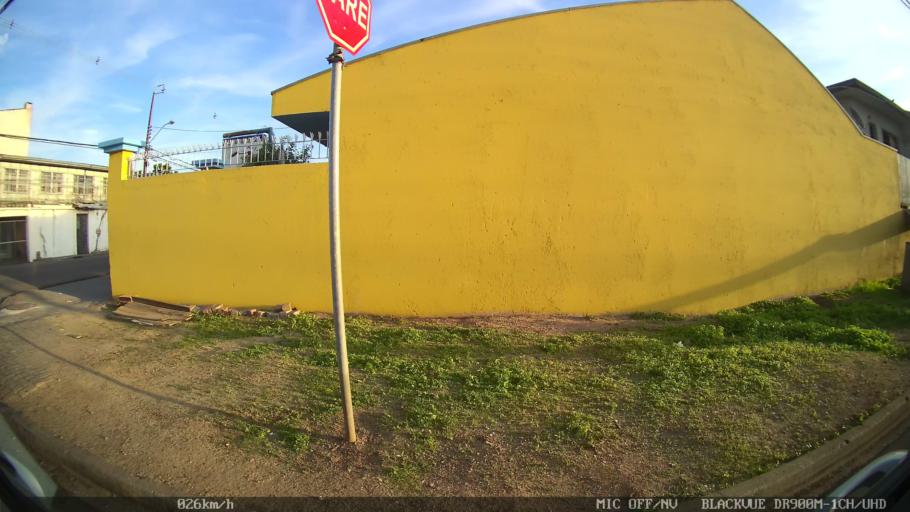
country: BR
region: Parana
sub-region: Pinhais
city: Pinhais
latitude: -25.4488
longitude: -49.1681
